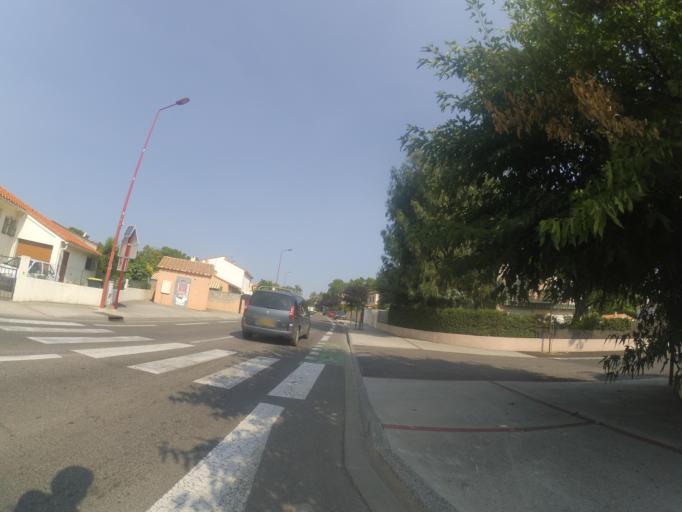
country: FR
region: Languedoc-Roussillon
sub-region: Departement des Pyrenees-Orientales
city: Toulouges
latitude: 42.6714
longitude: 2.8344
